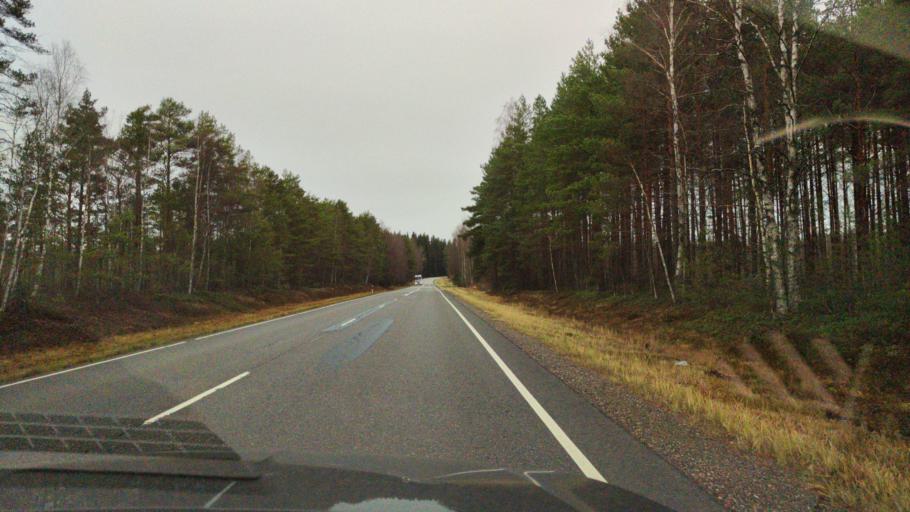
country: FI
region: Varsinais-Suomi
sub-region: Loimaa
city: Ylaene
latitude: 60.7498
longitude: 22.4270
